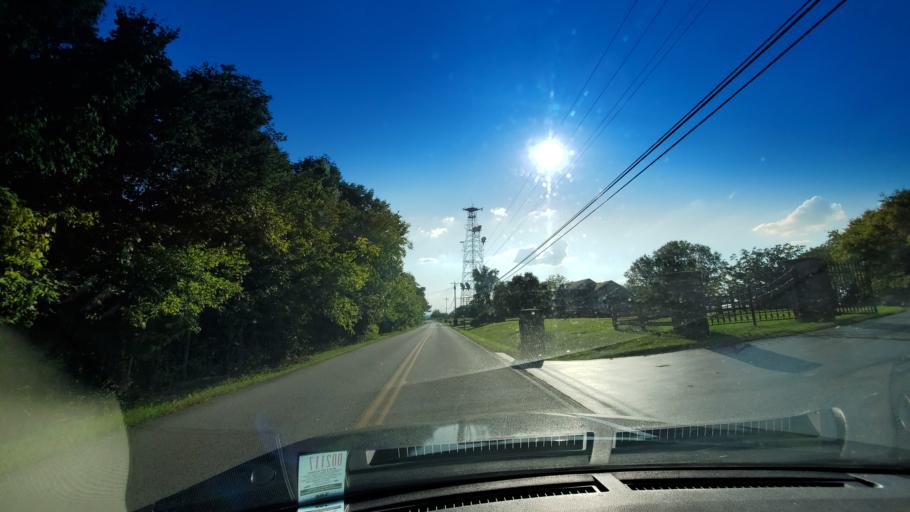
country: US
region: Tennessee
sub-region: Wilson County
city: Rural Hill
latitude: 36.1507
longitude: -86.3842
